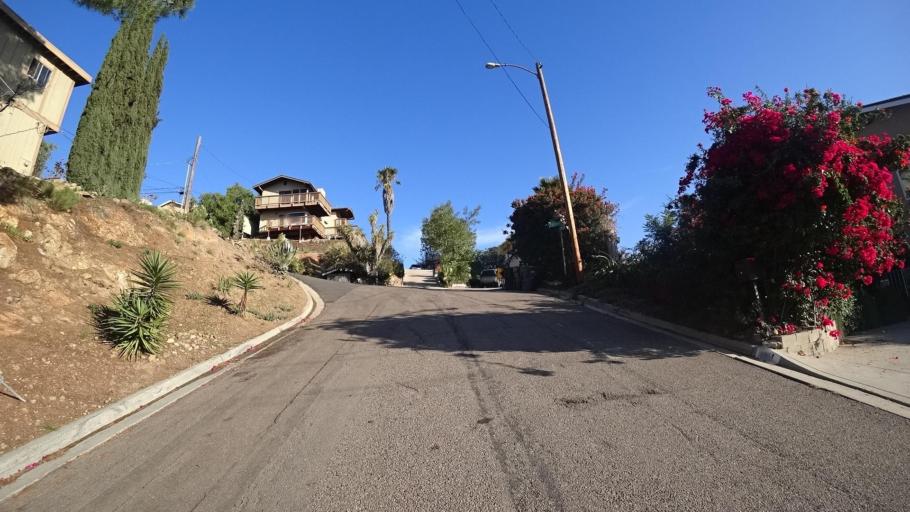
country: US
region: California
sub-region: San Diego County
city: La Presa
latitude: 32.7217
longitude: -116.9853
